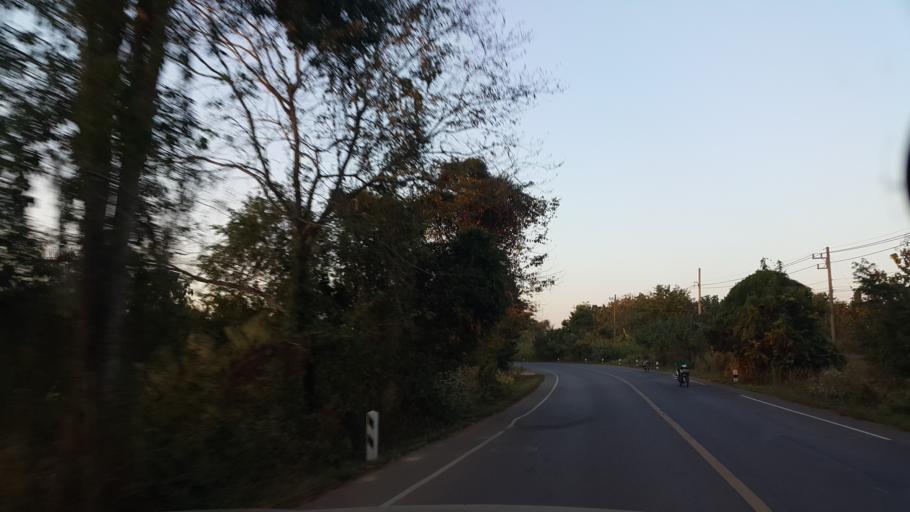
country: TH
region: Phrae
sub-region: Amphoe Wang Chin
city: Wang Chin
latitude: 17.8490
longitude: 99.6279
